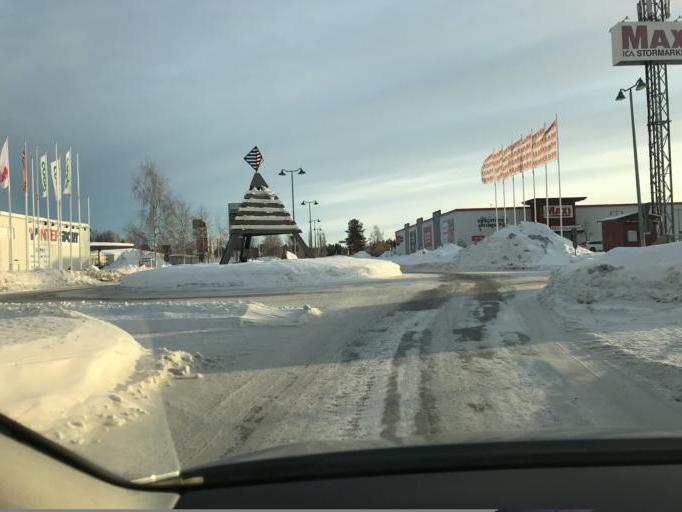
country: SE
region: Norrbotten
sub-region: Lulea Kommun
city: Gammelstad
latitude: 65.6177
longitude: 22.0452
